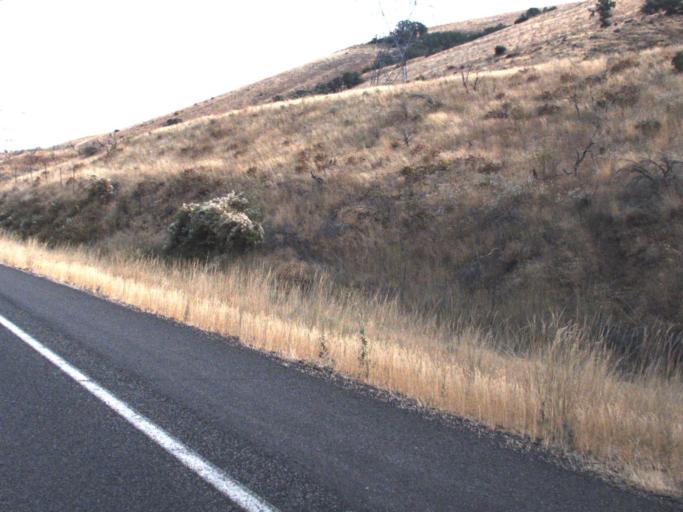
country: US
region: Washington
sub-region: Klickitat County
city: Goldendale
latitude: 46.0756
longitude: -120.5562
